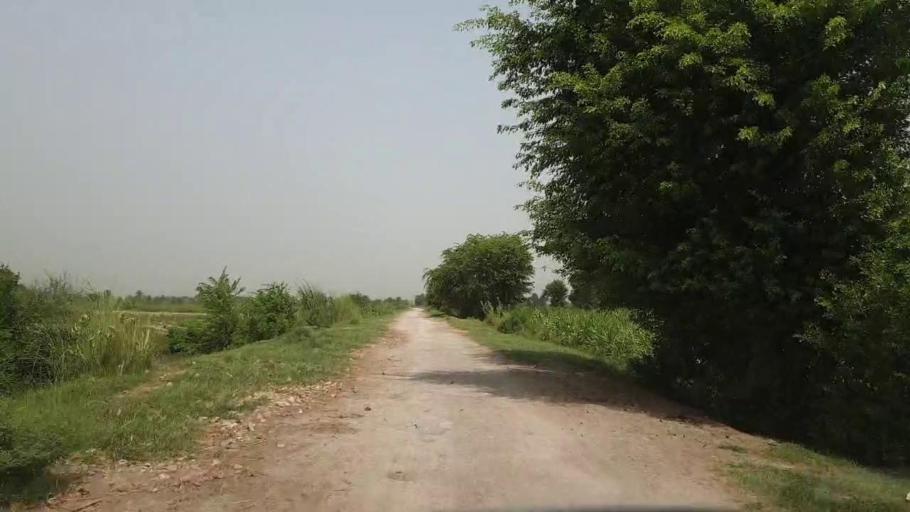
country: PK
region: Sindh
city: Gambat
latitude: 27.4521
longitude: 68.4418
